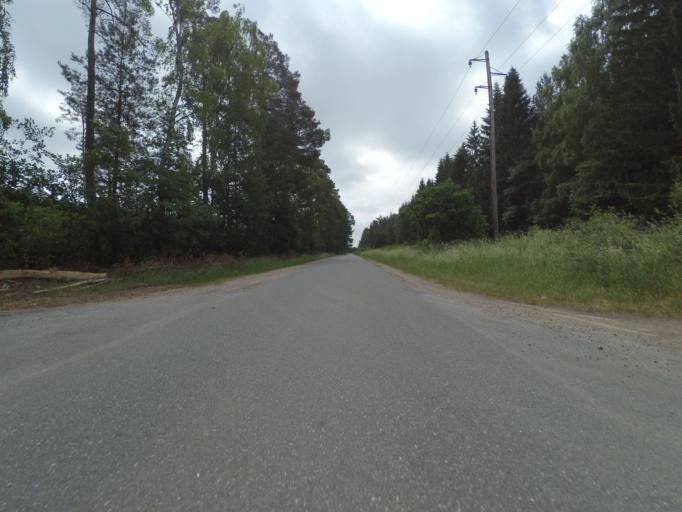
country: DE
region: Mecklenburg-Vorpommern
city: Malchow
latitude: 53.5469
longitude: 12.4193
